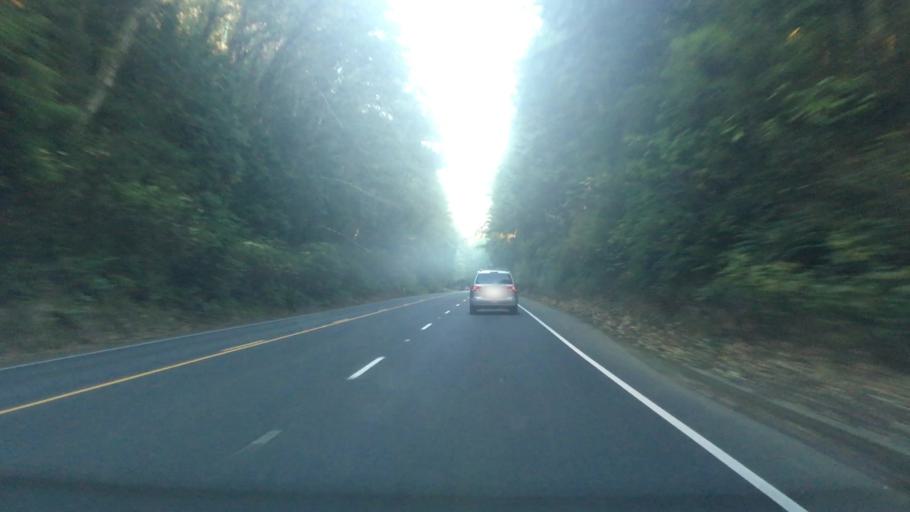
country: US
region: Oregon
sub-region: Clatsop County
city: Cannon Beach
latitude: 45.7875
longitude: -123.9590
